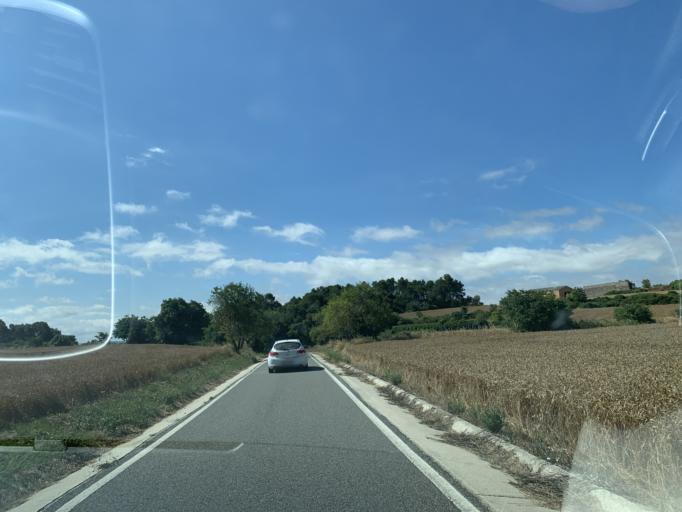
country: ES
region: Catalonia
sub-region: Provincia de Tarragona
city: Conesa
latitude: 41.5437
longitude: 1.3057
